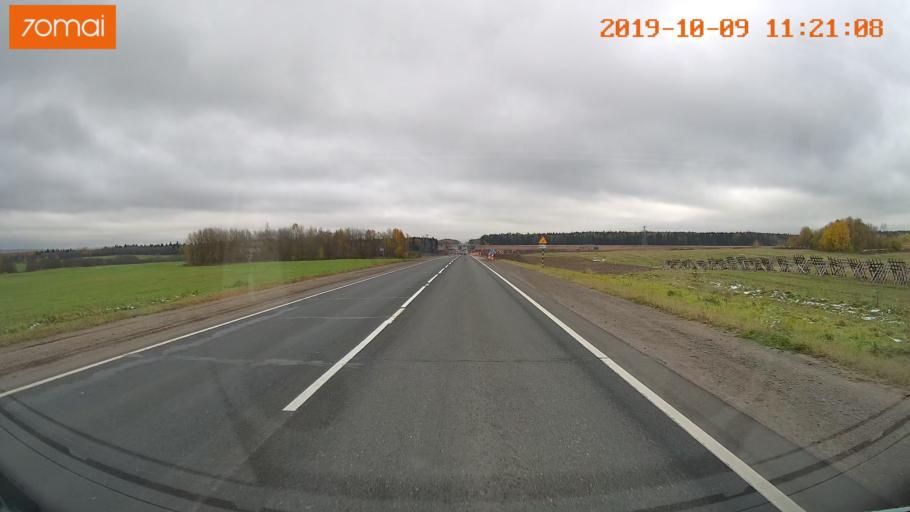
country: RU
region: Vologda
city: Vologda
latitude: 59.1421
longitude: 39.9467
